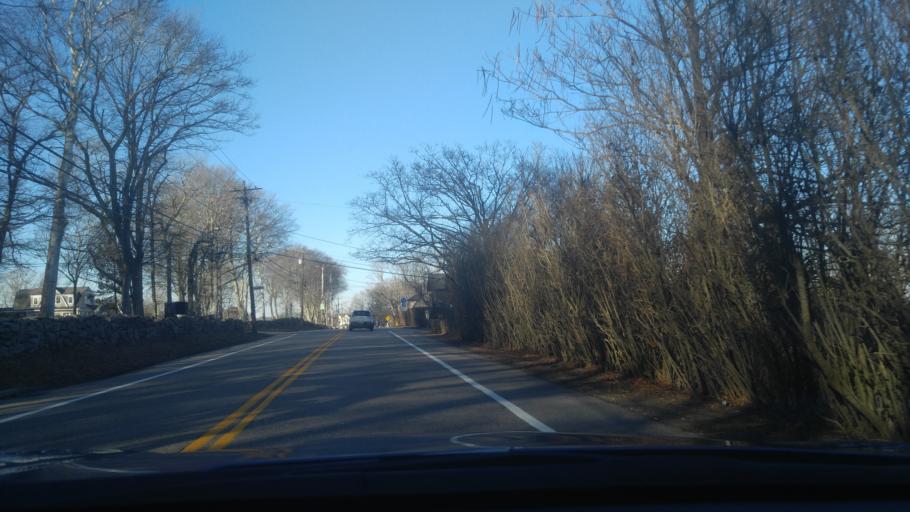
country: US
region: Rhode Island
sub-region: Washington County
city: Narragansett Pier
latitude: 41.4150
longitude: -71.4551
